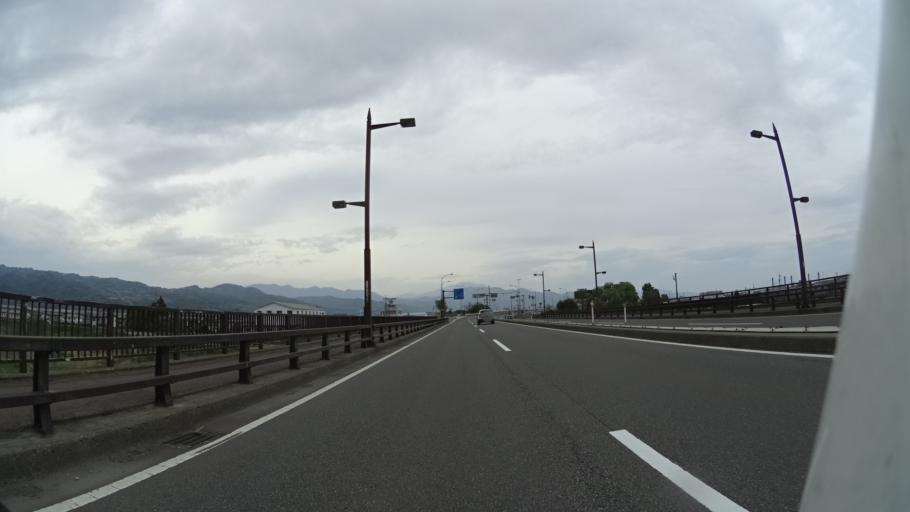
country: JP
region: Nagano
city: Nagano-shi
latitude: 36.5595
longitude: 138.1383
